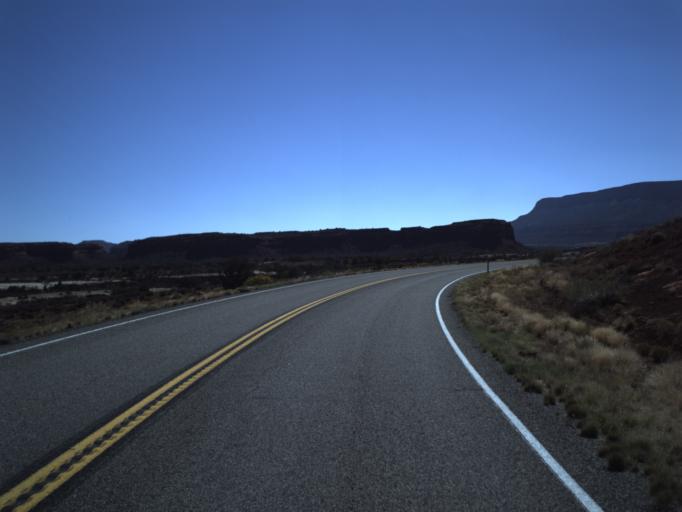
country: US
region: Utah
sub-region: San Juan County
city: Blanding
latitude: 37.7297
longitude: -110.2505
